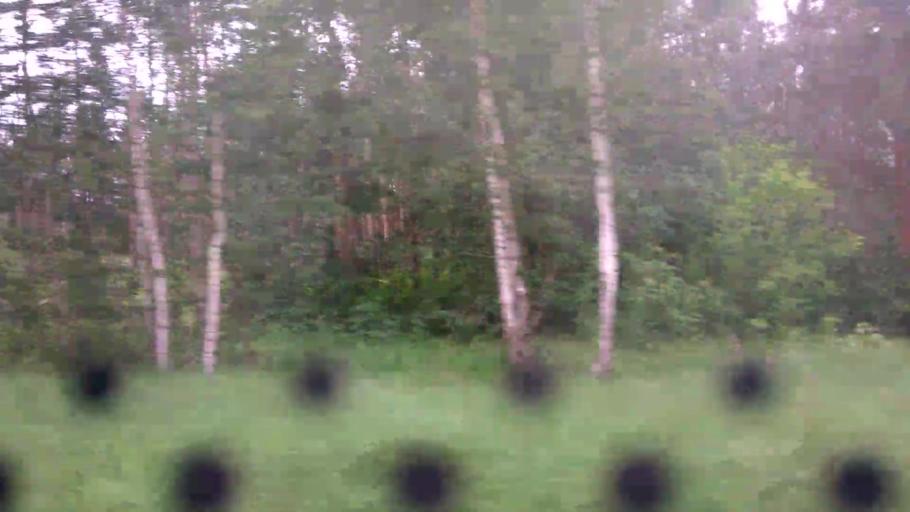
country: RU
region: Moskovskaya
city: Kolomna
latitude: 55.0533
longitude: 38.8689
